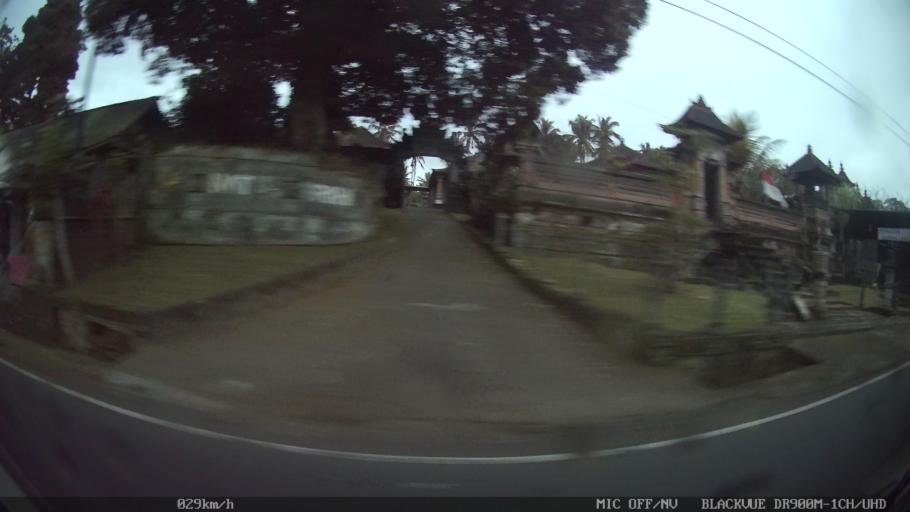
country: ID
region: Bali
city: Banjar Buahan
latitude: -8.4024
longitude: 115.2476
